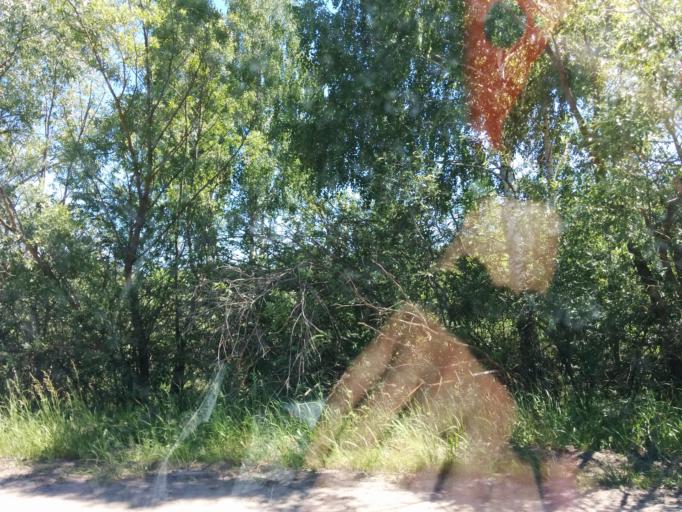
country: RU
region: Tambov
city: Morshansk
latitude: 53.6140
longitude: 41.8408
